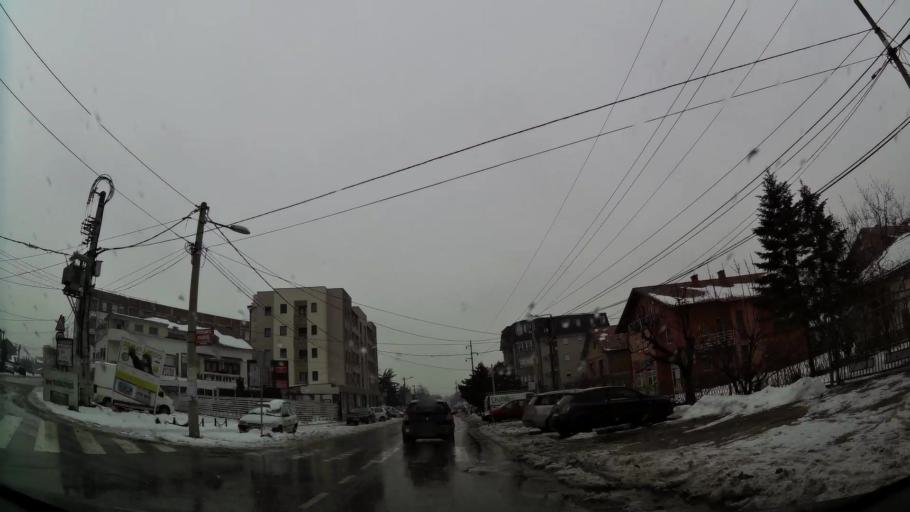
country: RS
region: Central Serbia
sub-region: Belgrade
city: Zemun
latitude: 44.8526
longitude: 20.3636
